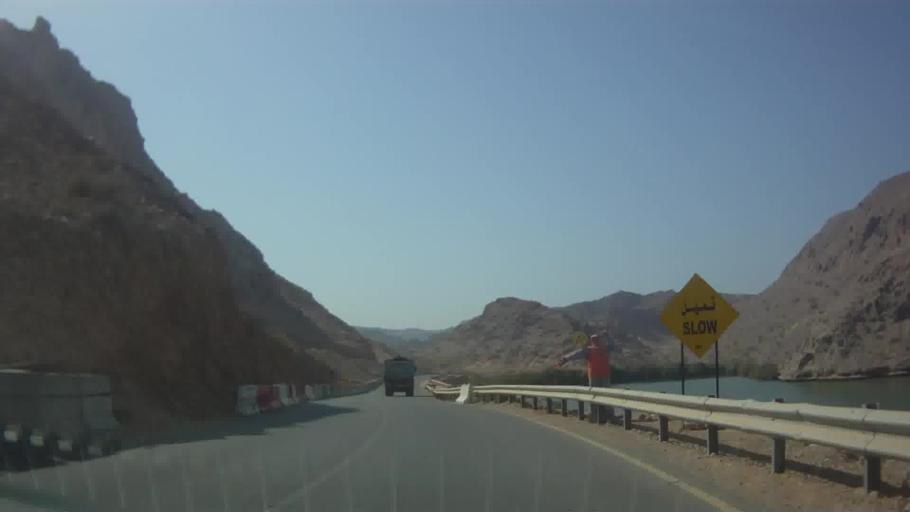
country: OM
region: Muhafazat Masqat
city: Muscat
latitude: 23.5125
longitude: 58.7219
